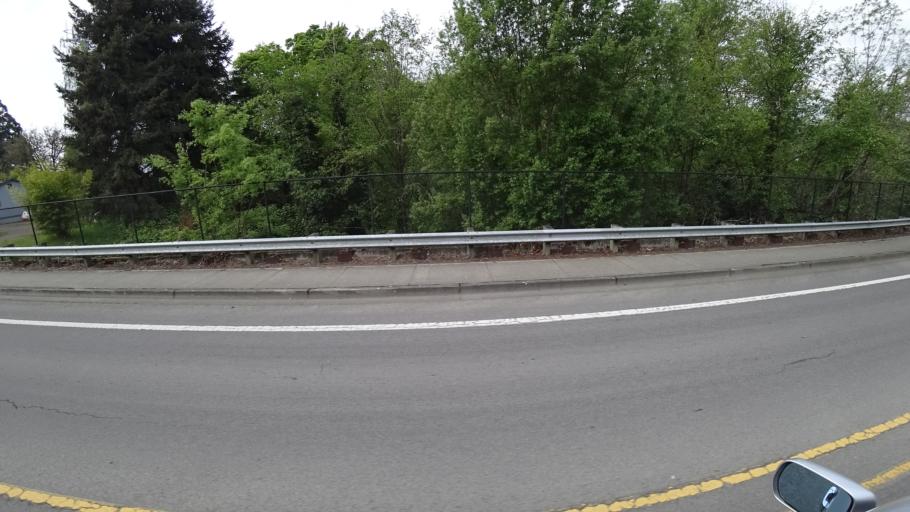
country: US
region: Oregon
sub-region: Washington County
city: Hillsboro
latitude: 45.5349
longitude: -122.9930
